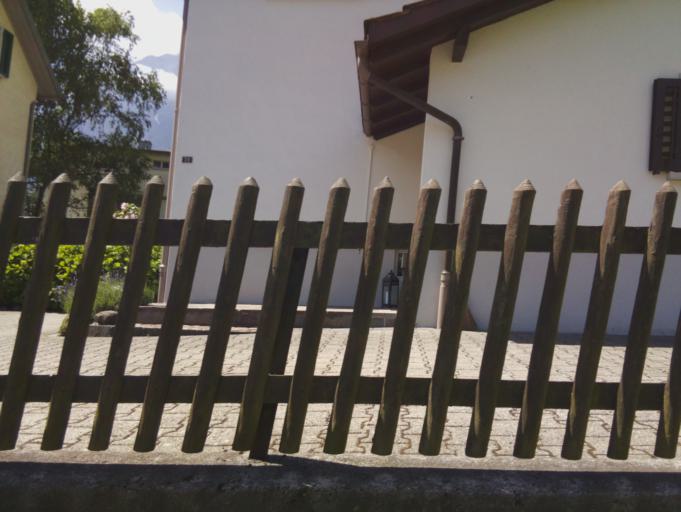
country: CH
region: Glarus
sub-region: Glarus
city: Netstal
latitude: 47.0598
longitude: 9.0507
